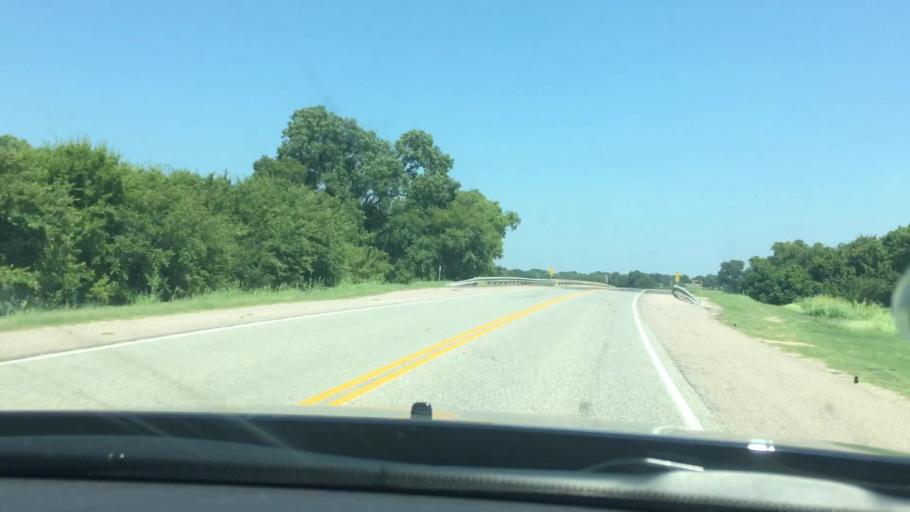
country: US
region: Oklahoma
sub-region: Johnston County
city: Tishomingo
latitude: 34.2496
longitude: -96.5495
